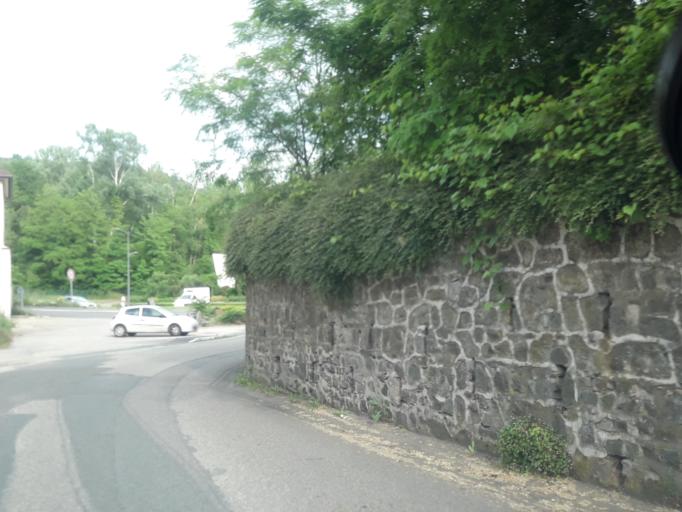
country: FR
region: Rhone-Alpes
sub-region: Departement du Rhone
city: Sain-Bel
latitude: 45.8181
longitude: 4.6032
